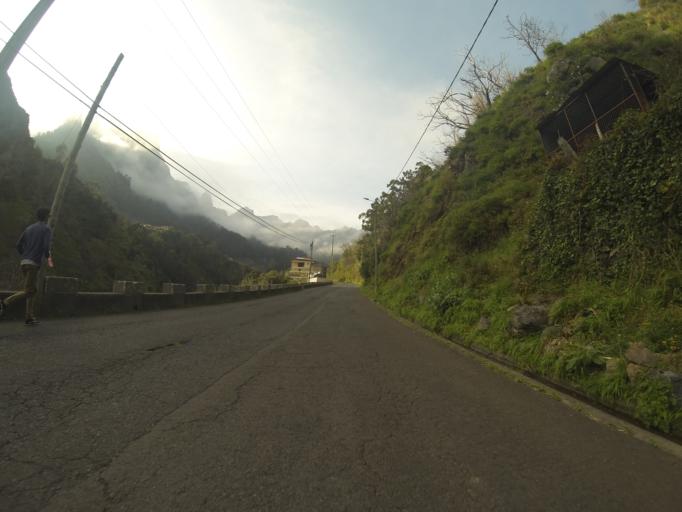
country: PT
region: Madeira
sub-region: Camara de Lobos
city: Curral das Freiras
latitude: 32.7294
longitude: -16.9674
